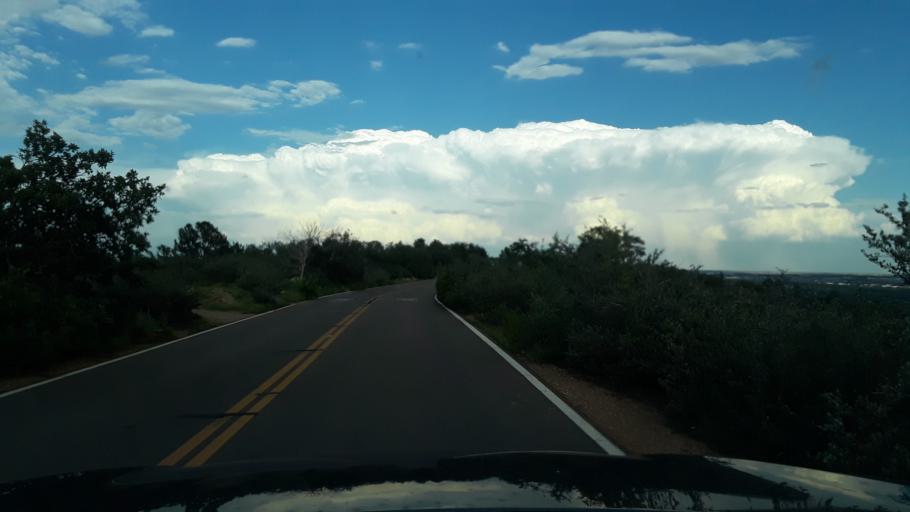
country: US
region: Colorado
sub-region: El Paso County
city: Colorado Springs
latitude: 38.8720
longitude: -104.7731
